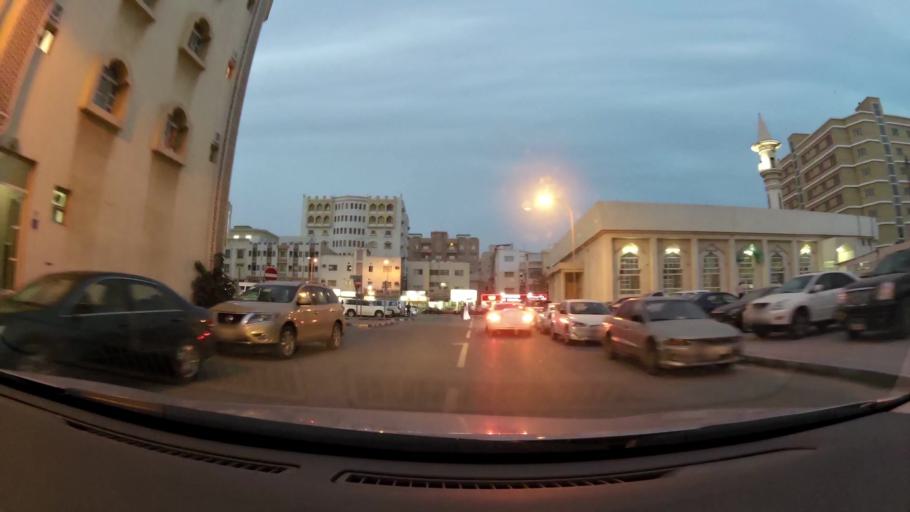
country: QA
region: Baladiyat ad Dawhah
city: Doha
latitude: 25.2696
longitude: 51.5207
